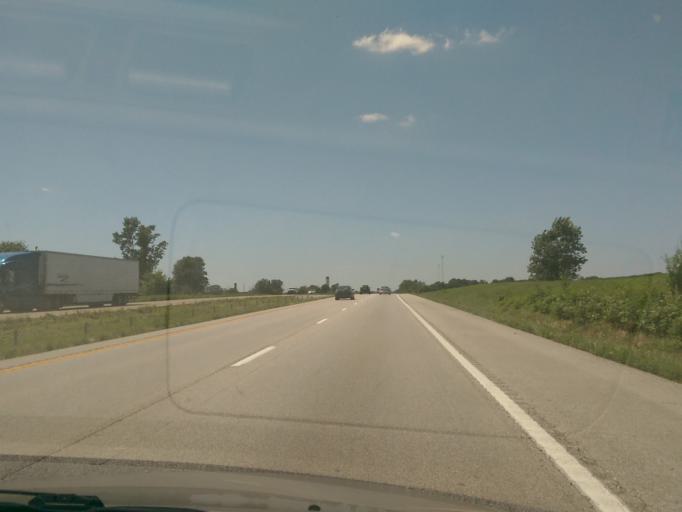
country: US
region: Missouri
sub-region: Cooper County
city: Boonville
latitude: 38.9352
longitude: -92.8917
